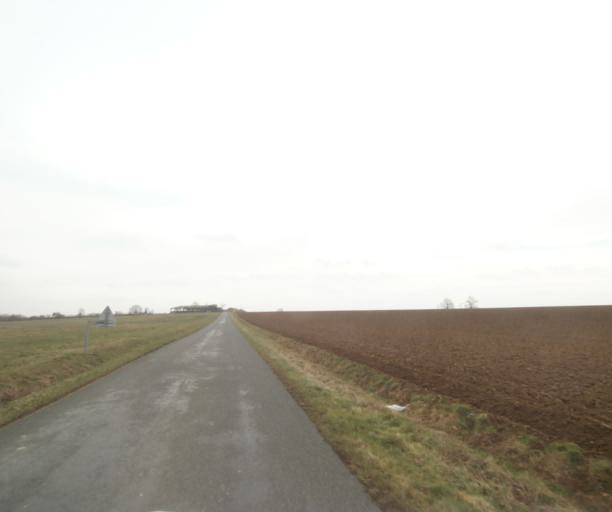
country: FR
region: Champagne-Ardenne
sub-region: Departement de la Marne
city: Pargny-sur-Saulx
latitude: 48.7387
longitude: 4.8273
